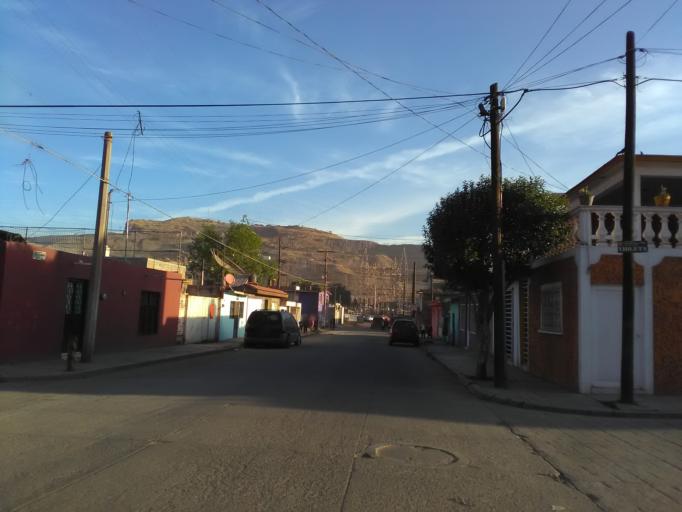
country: MX
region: Durango
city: Victoria de Durango
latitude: 24.0456
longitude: -104.6688
